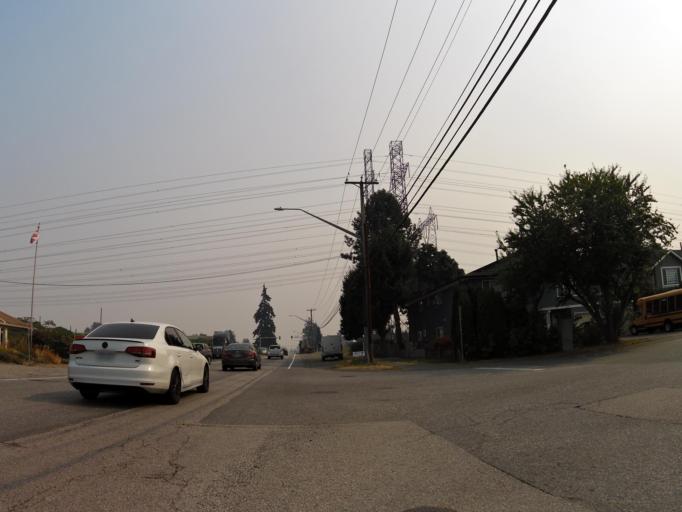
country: CA
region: British Columbia
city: Delta
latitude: 49.1483
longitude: -122.8759
